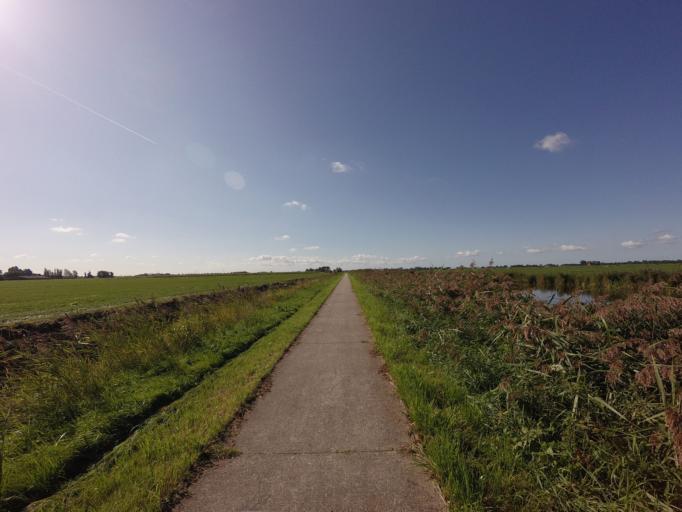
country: NL
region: Friesland
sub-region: Gemeente Boarnsterhim
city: Reduzum
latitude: 53.1359
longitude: 5.7595
